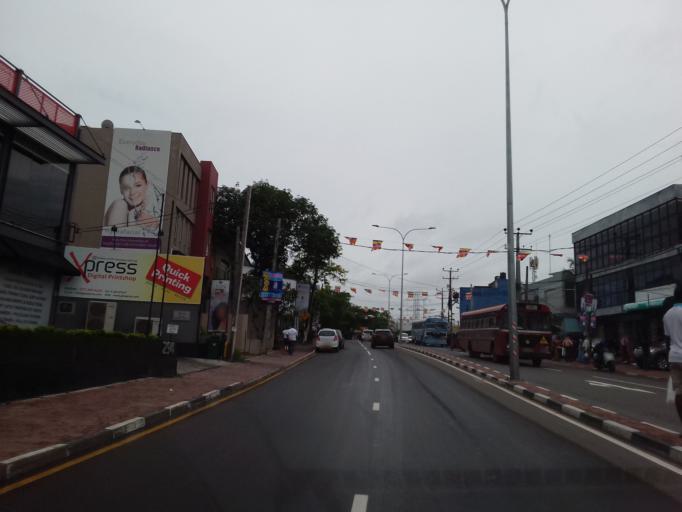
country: LK
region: Western
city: Battaramulla South
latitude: 6.8952
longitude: 79.9240
